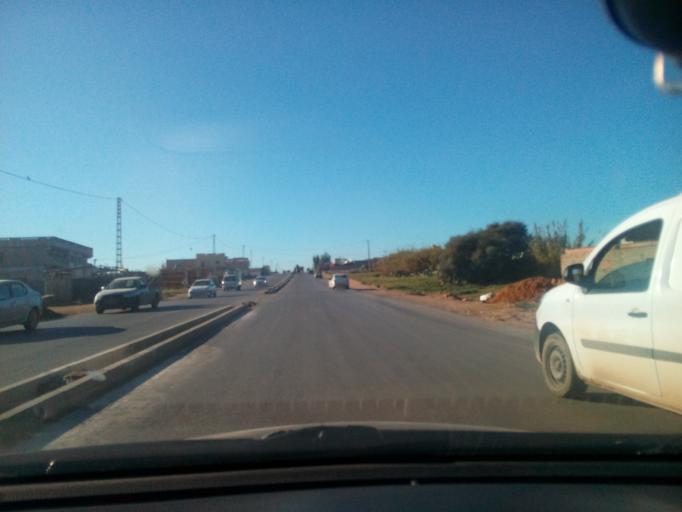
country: DZ
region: Mostaganem
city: Mostaganem
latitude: 35.9089
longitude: 0.1660
